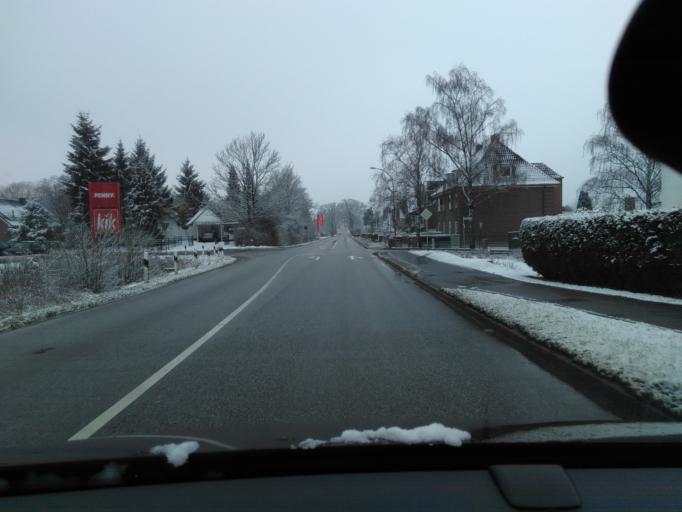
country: DE
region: Schleswig-Holstein
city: Ahrensbok
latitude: 54.0153
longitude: 10.5699
